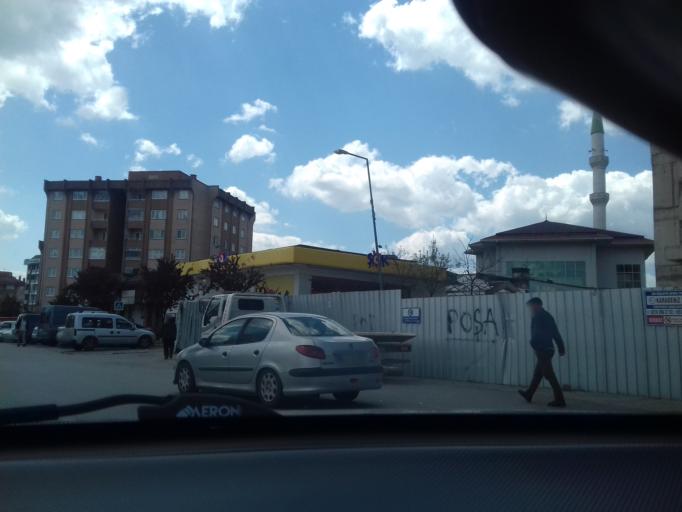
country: TR
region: Istanbul
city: Pendik
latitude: 40.9087
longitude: 29.2787
